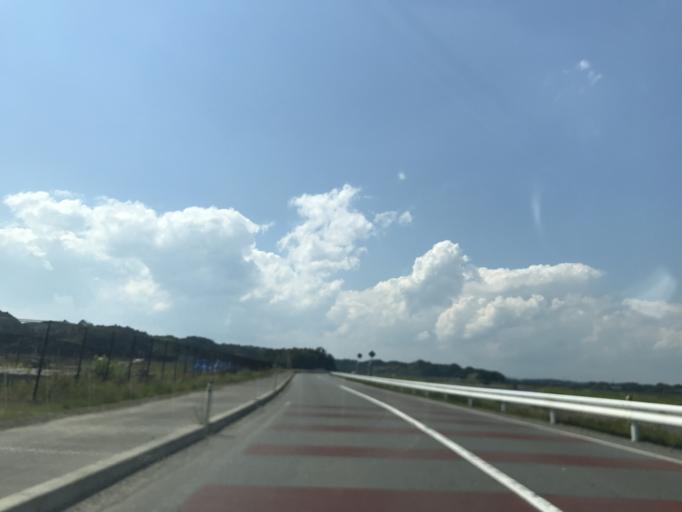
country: JP
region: Miyagi
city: Yamoto
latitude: 38.3889
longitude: 141.1612
